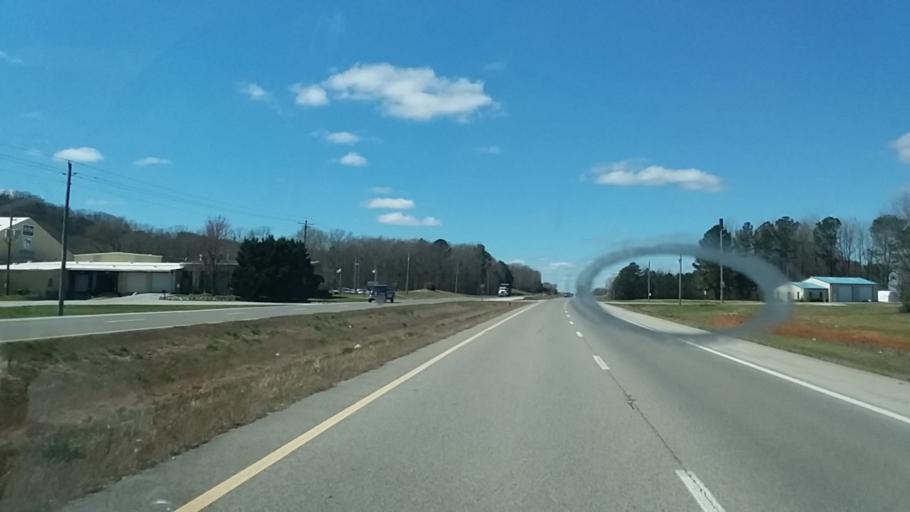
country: US
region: Alabama
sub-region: Colbert County
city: Cherokee
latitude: 34.7356
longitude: -87.9026
